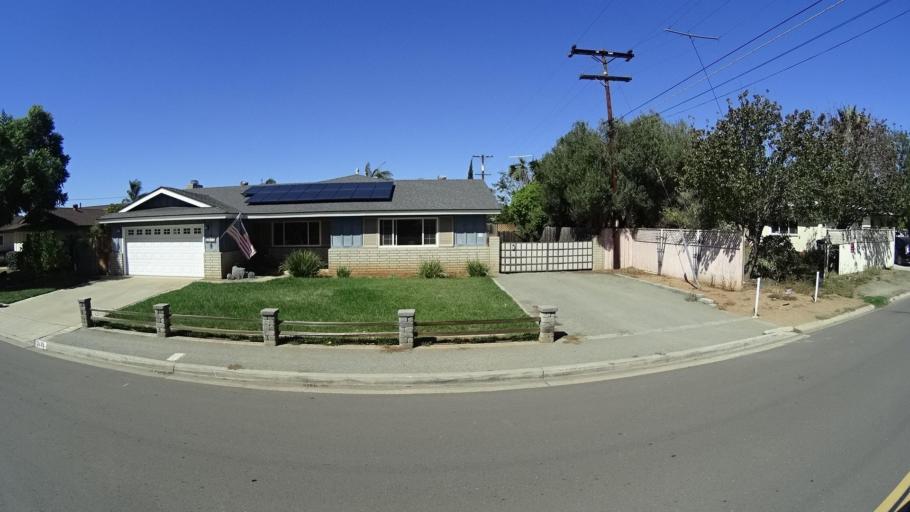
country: US
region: California
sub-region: San Diego County
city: Bonita
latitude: 32.6551
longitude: -117.0581
